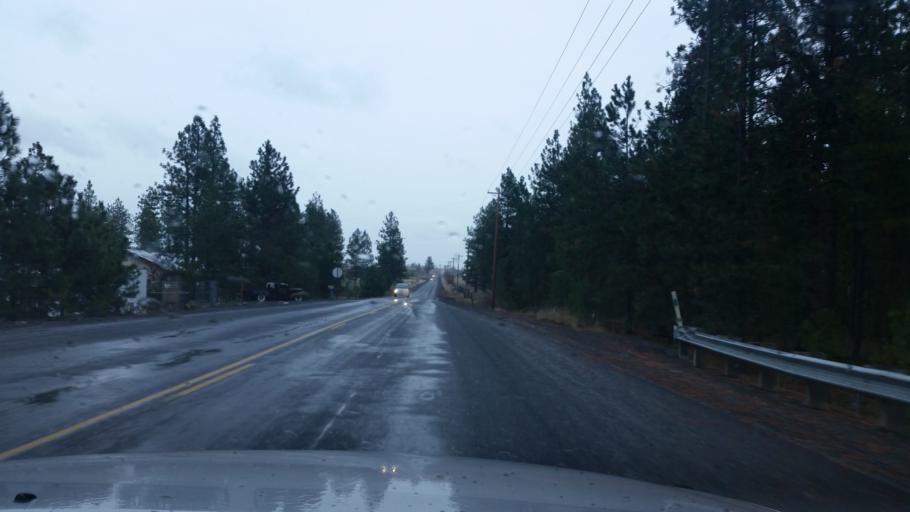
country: US
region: Washington
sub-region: Spokane County
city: Airway Heights
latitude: 47.6719
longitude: -117.5844
